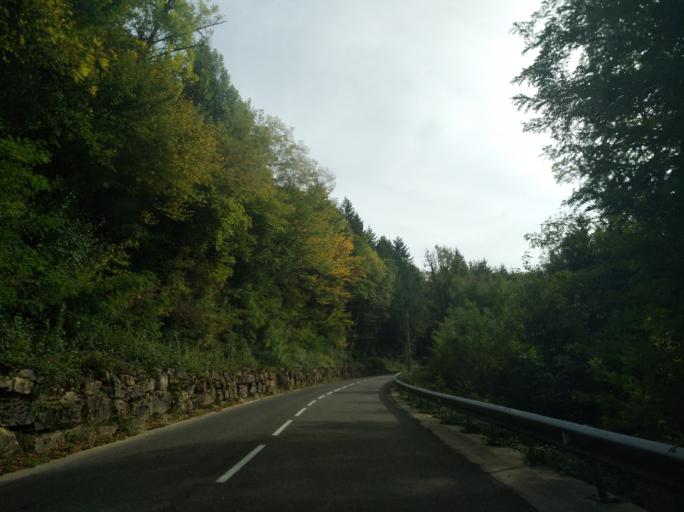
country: FR
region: Bourgogne
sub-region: Departement de Saone-et-Loire
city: Cuiseaux
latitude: 46.4578
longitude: 5.3918
